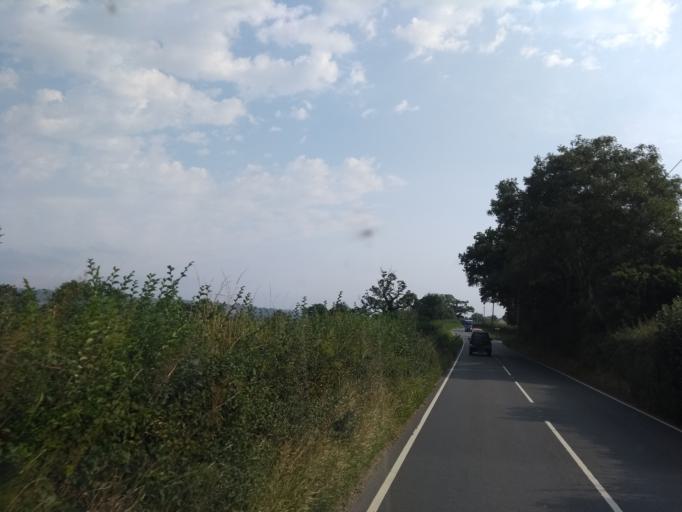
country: GB
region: England
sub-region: Devon
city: Axminster
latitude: 50.7626
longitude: -3.0136
